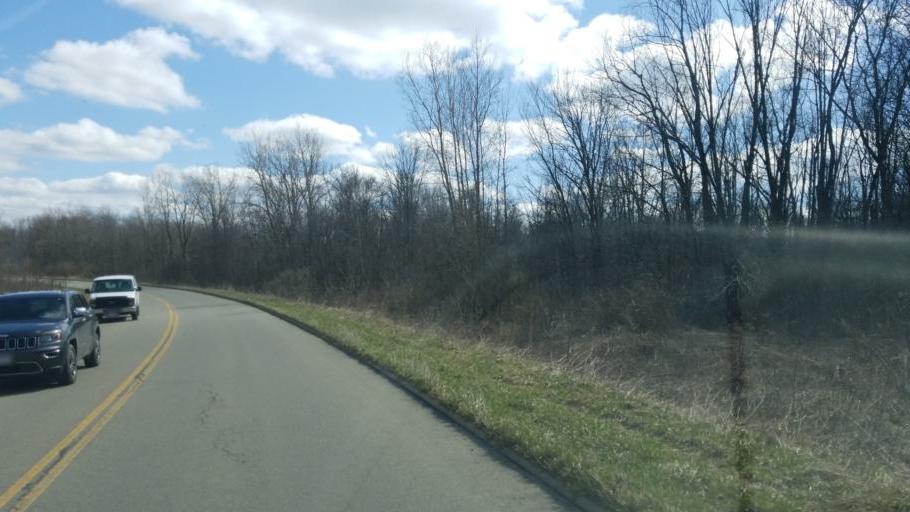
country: US
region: Ohio
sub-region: Richland County
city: Mansfield
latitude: 40.7951
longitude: -82.5406
